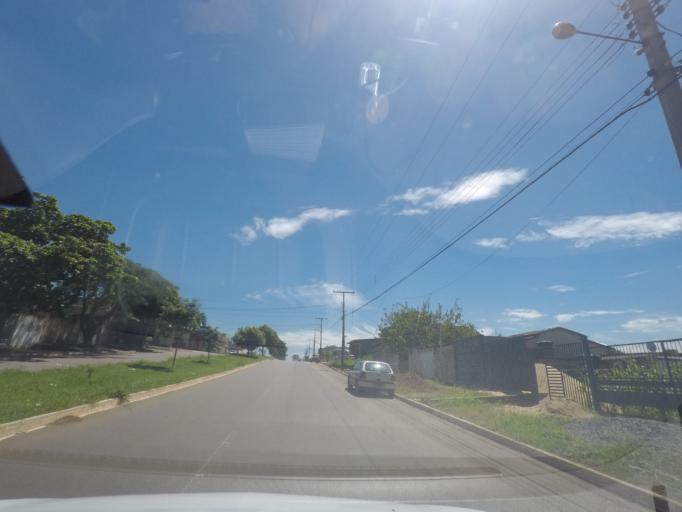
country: BR
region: Goias
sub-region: Aparecida De Goiania
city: Aparecida de Goiania
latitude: -16.7724
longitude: -49.3246
